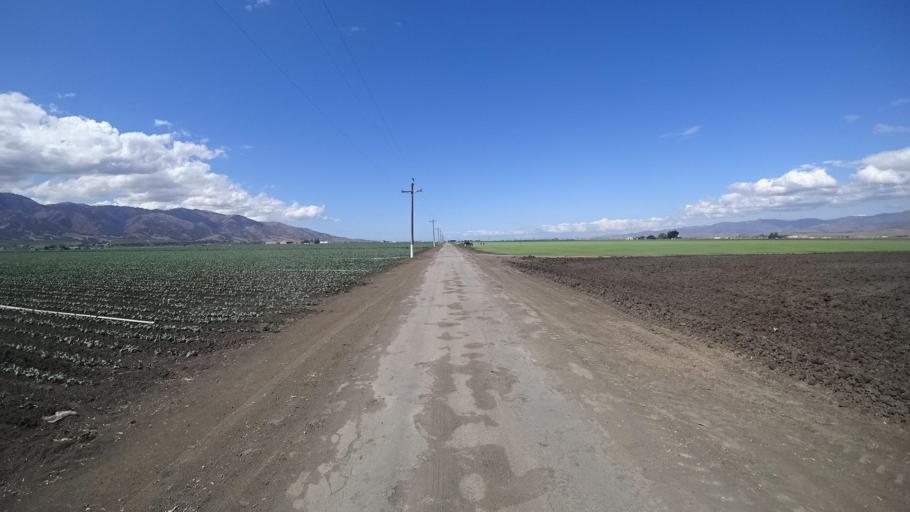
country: US
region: California
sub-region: Monterey County
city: Gonzales
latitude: 36.5118
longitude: -121.4779
